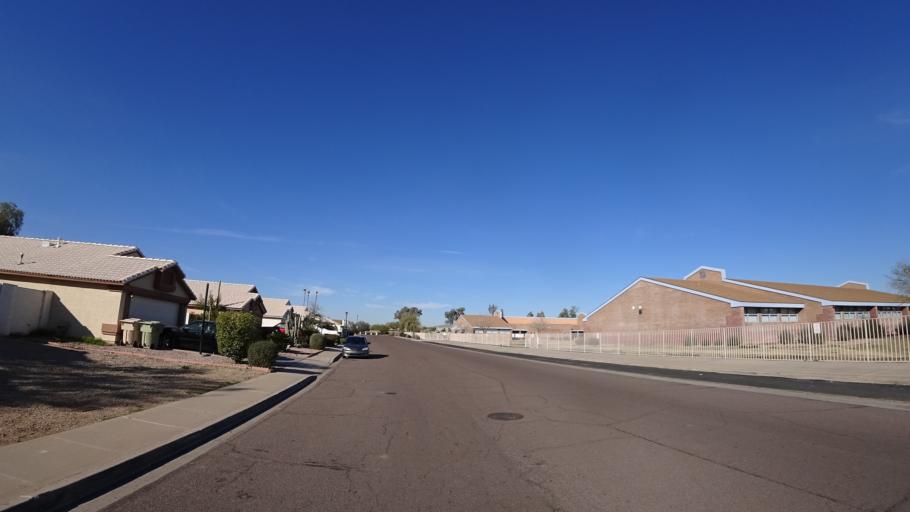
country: US
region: Arizona
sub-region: Maricopa County
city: Glendale
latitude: 33.5219
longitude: -112.2249
